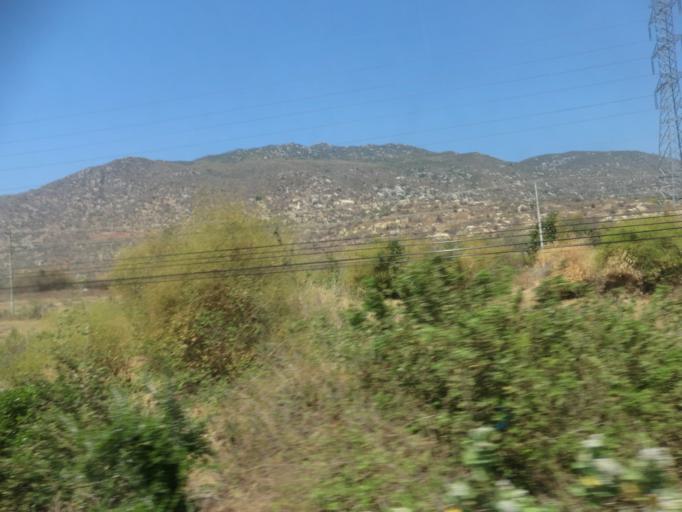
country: VN
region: Ninh Thuan
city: Phuoc Dan
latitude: 11.3677
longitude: 108.8784
